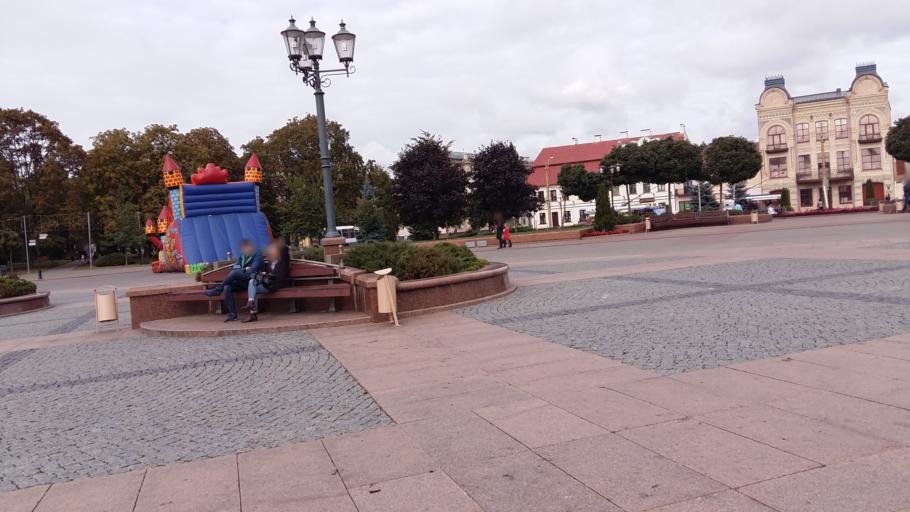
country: BY
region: Grodnenskaya
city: Hrodna
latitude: 53.6779
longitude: 23.8296
